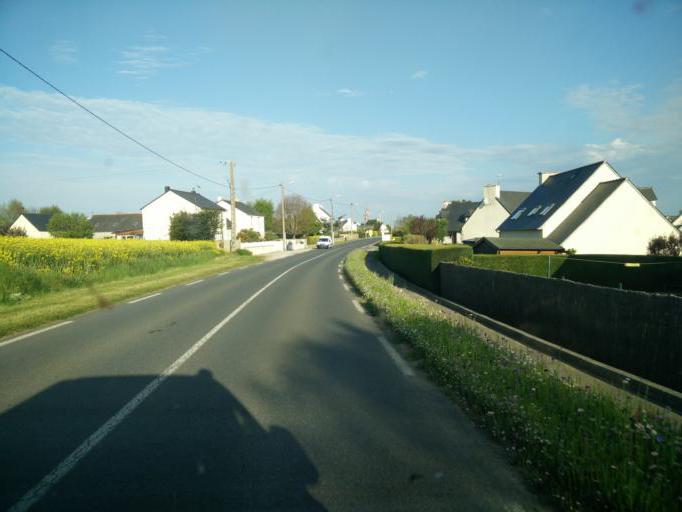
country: FR
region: Brittany
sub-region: Departement des Cotes-d'Armor
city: Erquy
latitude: 48.6265
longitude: -2.4516
